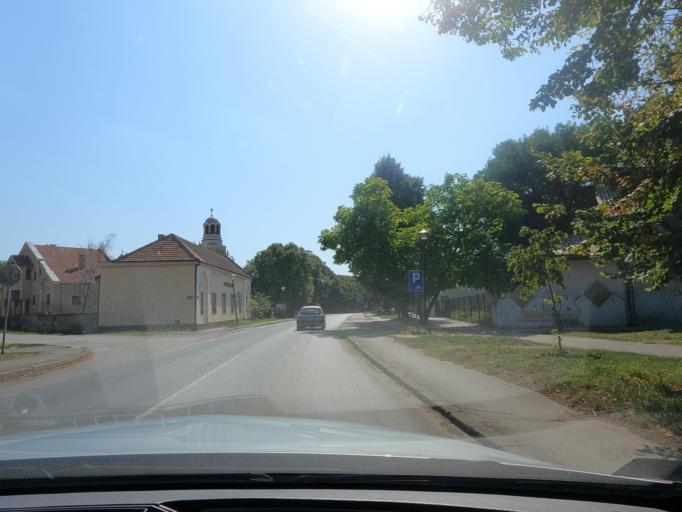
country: RS
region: Autonomna Pokrajina Vojvodina
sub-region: Severnobacki Okrug
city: Backa Topola
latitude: 45.8163
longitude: 19.6451
